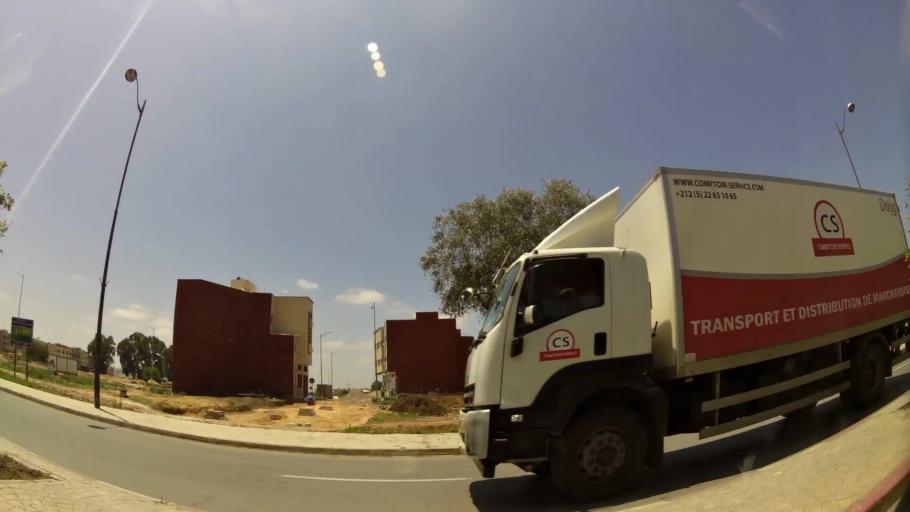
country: MA
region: Fes-Boulemane
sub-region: Fes
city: Fes
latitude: 34.0414
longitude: -5.0353
